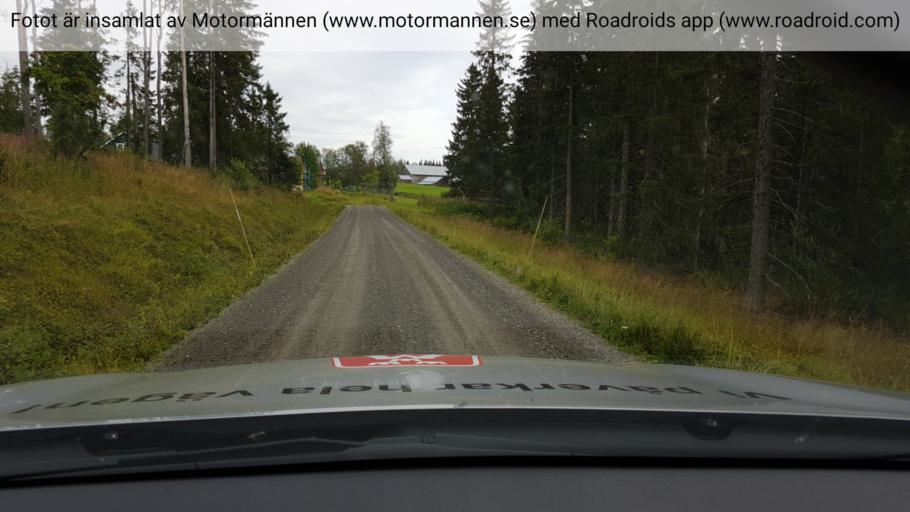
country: SE
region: Jaemtland
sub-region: Krokoms Kommun
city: Valla
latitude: 63.5275
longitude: 13.8832
